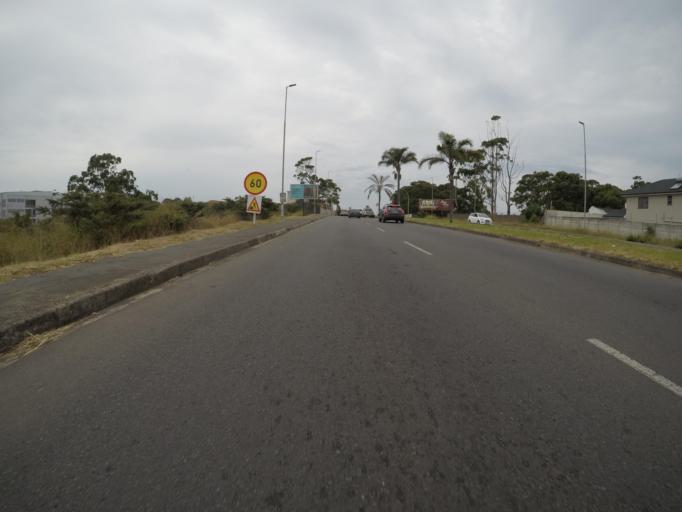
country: ZA
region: Eastern Cape
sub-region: Buffalo City Metropolitan Municipality
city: East London
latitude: -32.9967
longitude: 27.8880
